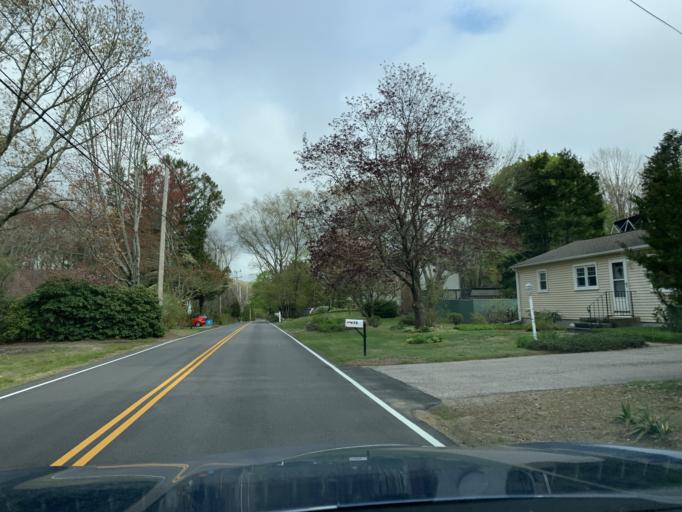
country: US
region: Rhode Island
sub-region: Washington County
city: North Kingstown
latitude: 41.6034
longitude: -71.4832
